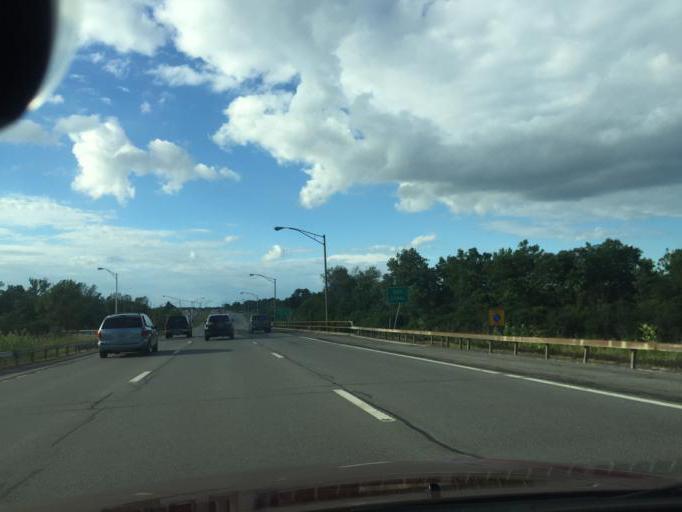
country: US
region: New York
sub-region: Monroe County
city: North Gates
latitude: 43.1729
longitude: -77.6831
